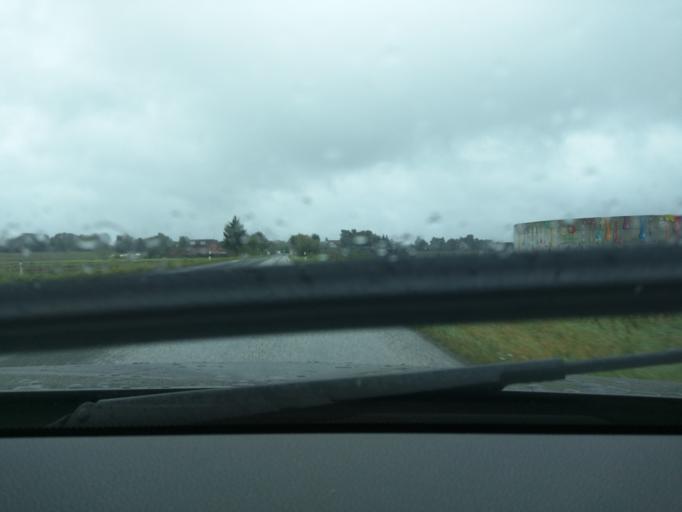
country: DE
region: Schleswig-Holstein
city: Lutau
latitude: 53.4283
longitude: 10.5422
